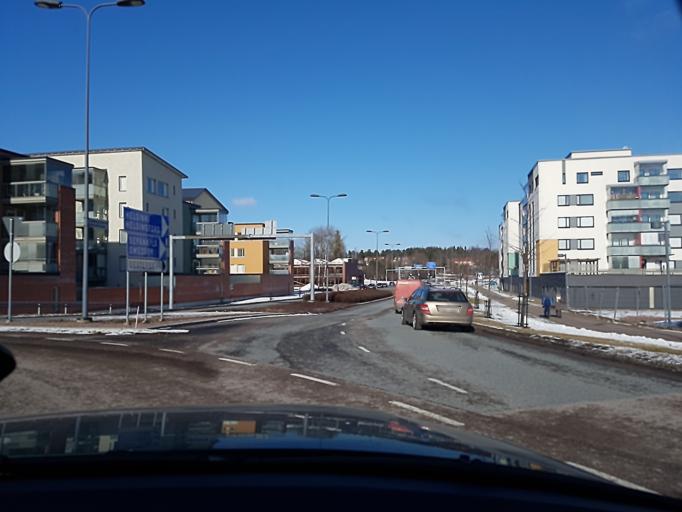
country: FI
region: Uusimaa
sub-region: Helsinki
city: Kirkkonummi
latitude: 60.1221
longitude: 24.4421
